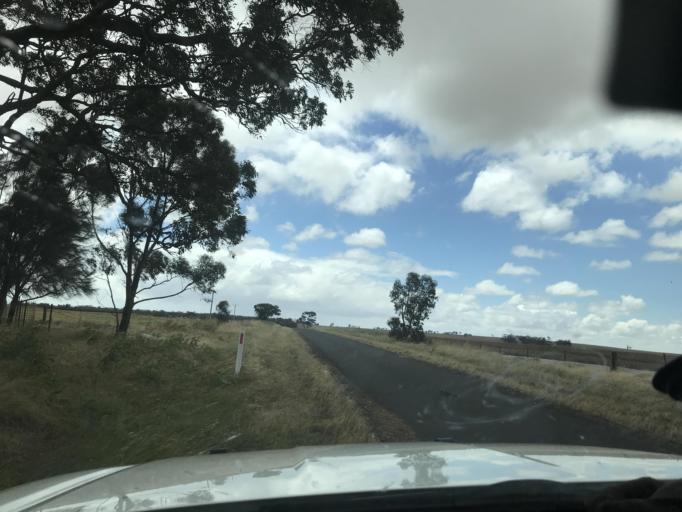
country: AU
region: South Australia
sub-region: Tatiara
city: Bordertown
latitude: -36.4113
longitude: 141.3304
